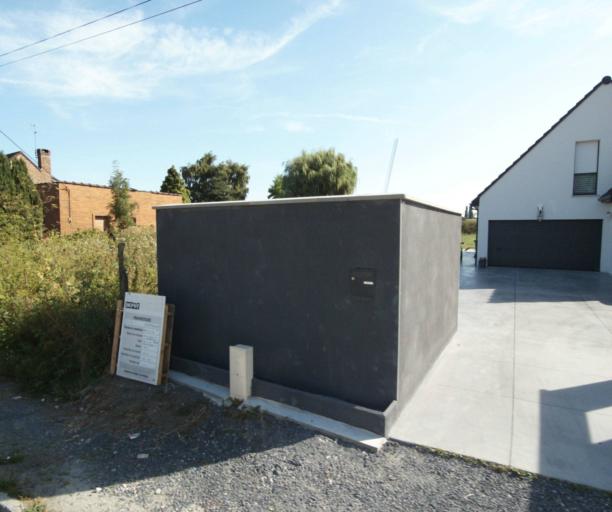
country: FR
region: Nord-Pas-de-Calais
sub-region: Departement du Nord
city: Halluin
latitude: 50.7693
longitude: 3.1418
